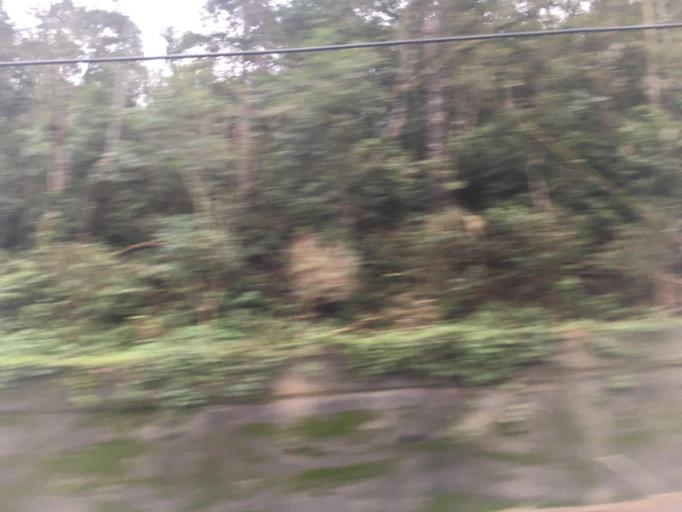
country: TW
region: Taiwan
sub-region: Miaoli
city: Miaoli
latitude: 24.4188
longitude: 120.7580
